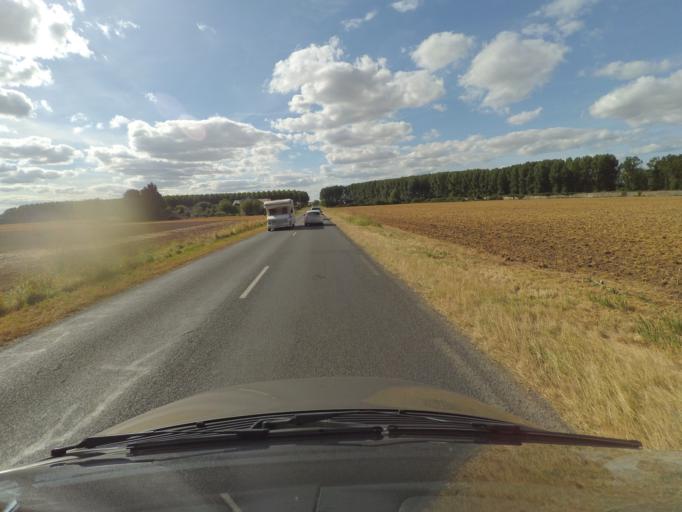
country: FR
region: Centre
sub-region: Departement d'Indre-et-Loire
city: Richelieu
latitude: 46.9950
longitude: 0.3237
